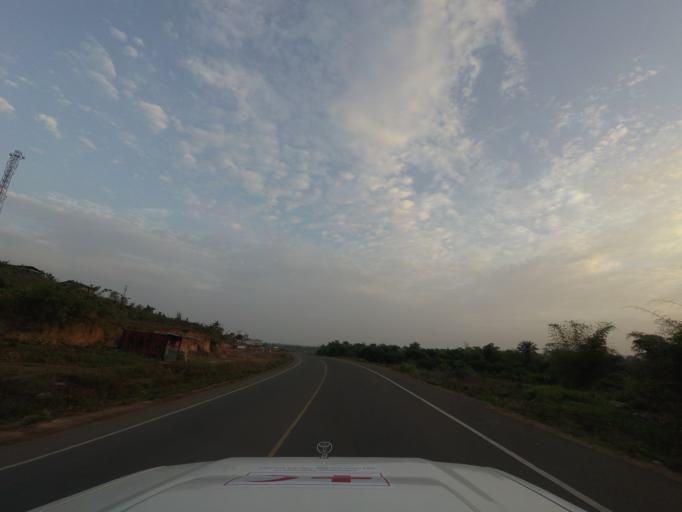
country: LR
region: Montserrado
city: Bensonville City
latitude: 6.3357
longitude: -10.6586
